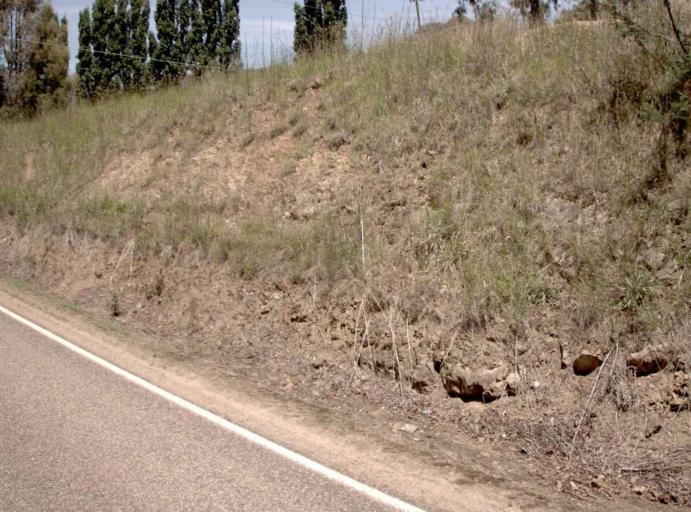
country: AU
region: Victoria
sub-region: East Gippsland
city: Bairnsdale
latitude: -37.3727
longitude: 147.8373
